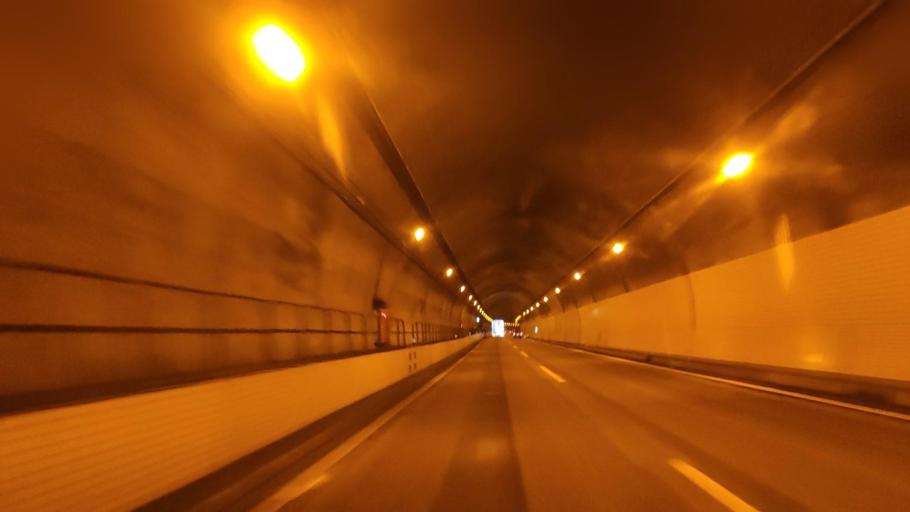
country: JP
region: Niigata
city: Joetsu
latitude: 37.1624
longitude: 138.0951
